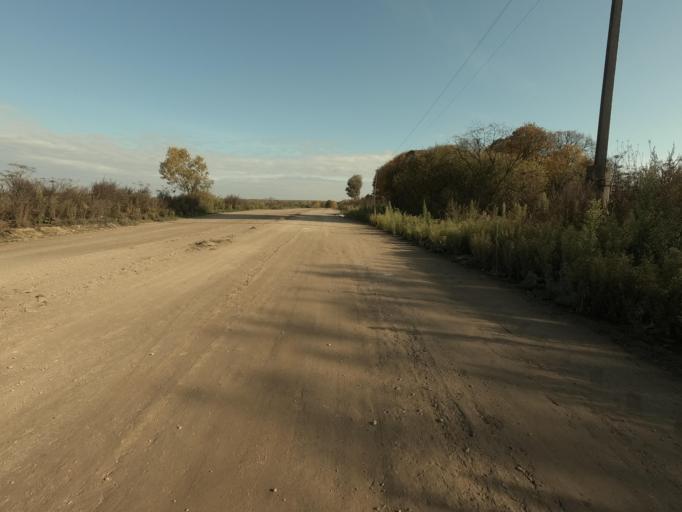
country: RU
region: Novgorod
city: Batetskiy
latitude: 58.8106
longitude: 30.6923
